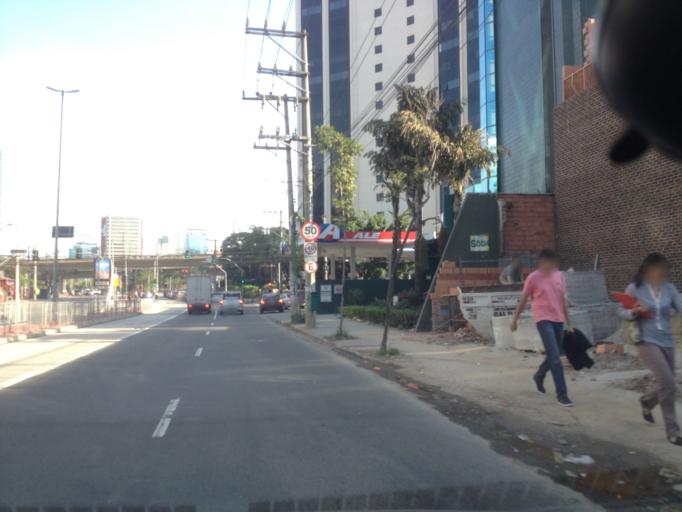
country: BR
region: Sao Paulo
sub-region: Sao Paulo
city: Sao Paulo
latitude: -23.5950
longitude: -46.6905
